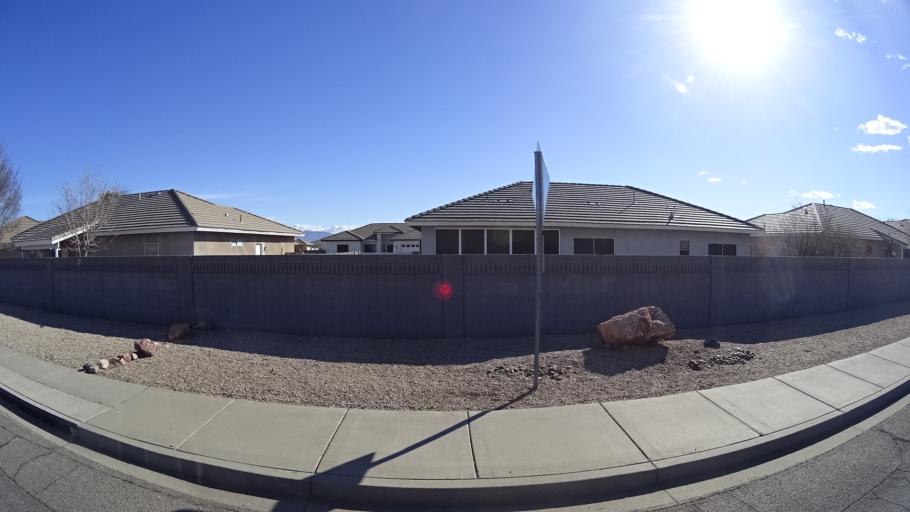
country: US
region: Arizona
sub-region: Mohave County
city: New Kingman-Butler
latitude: 35.2352
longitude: -114.0248
